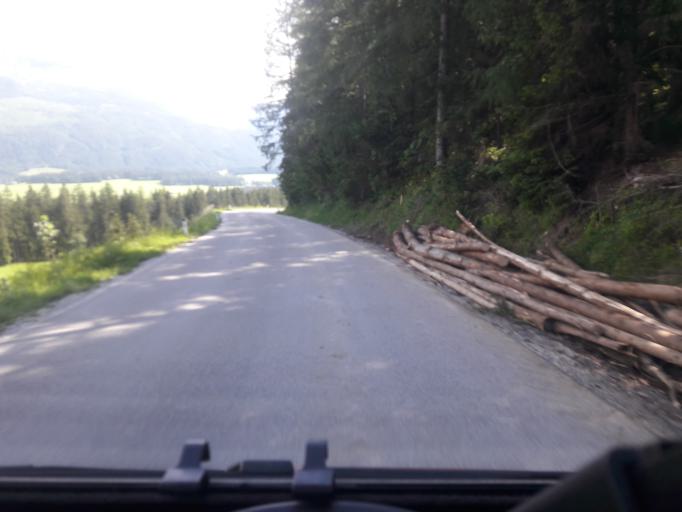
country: AT
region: Styria
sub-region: Politischer Bezirk Liezen
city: Tauplitz
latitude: 47.5678
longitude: 13.9571
